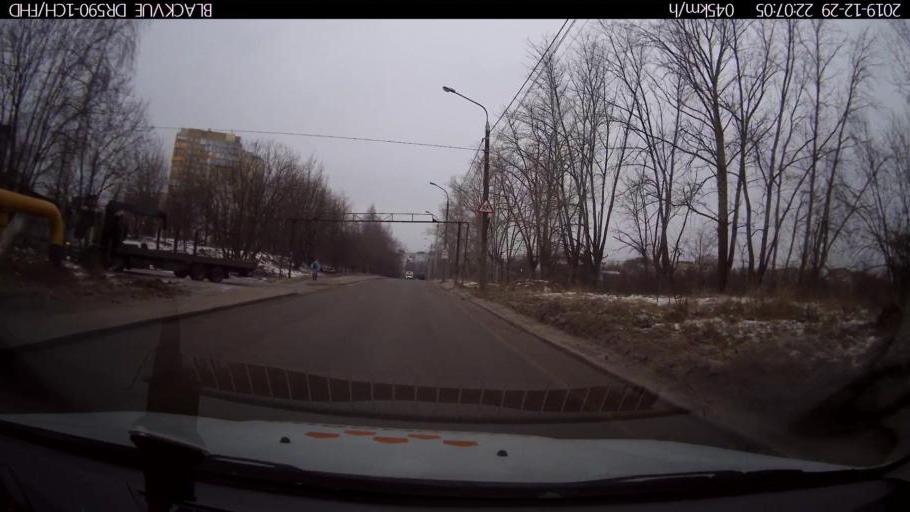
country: RU
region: Nizjnij Novgorod
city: Nizhniy Novgorod
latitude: 56.2259
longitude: 43.9513
